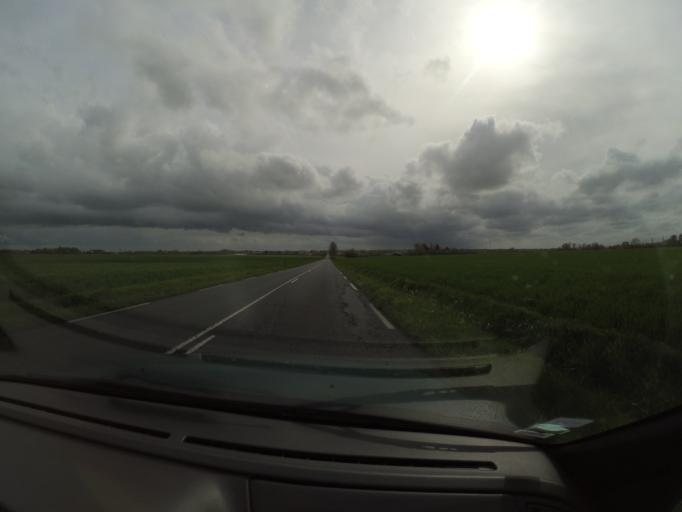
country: FR
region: Pays de la Loire
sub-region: Departement de Maine-et-Loire
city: Landemont
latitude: 47.2511
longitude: -1.2071
